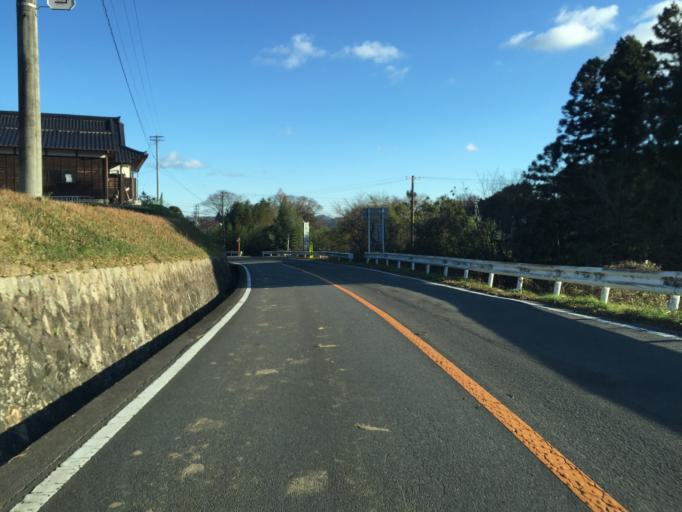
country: JP
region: Fukushima
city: Iwaki
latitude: 37.1424
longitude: 140.8390
